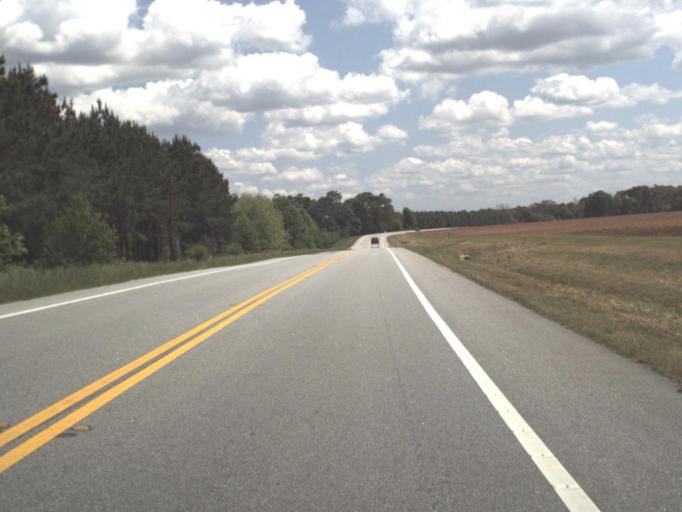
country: US
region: Alabama
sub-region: Escambia County
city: Atmore
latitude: 30.8844
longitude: -87.4500
